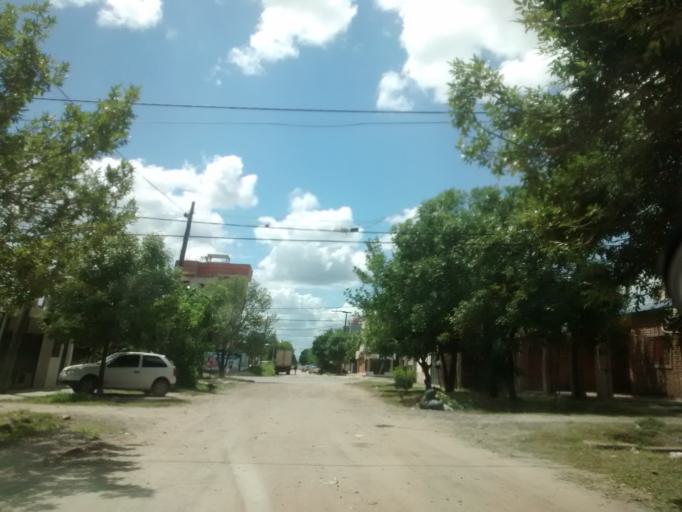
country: AR
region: Chaco
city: Resistencia
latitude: -27.4590
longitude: -59.0075
